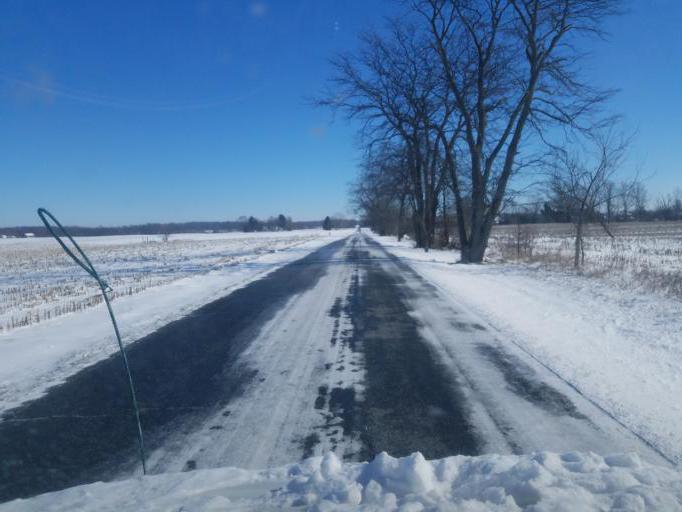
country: US
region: Ohio
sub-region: Delaware County
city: Delaware
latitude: 40.2874
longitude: -82.9964
